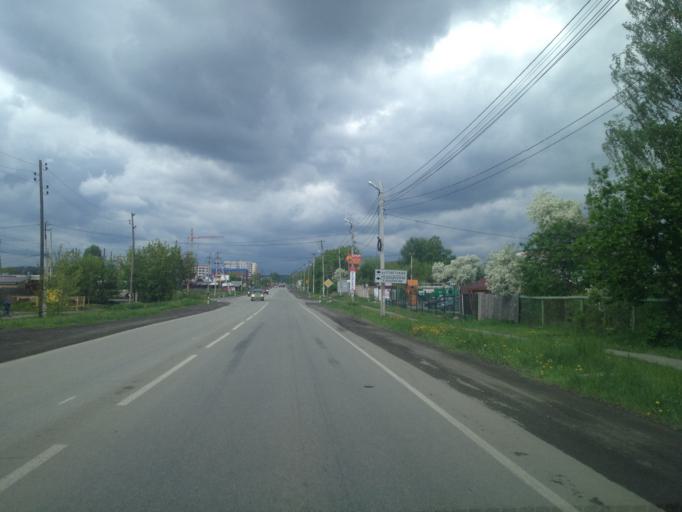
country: RU
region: Sverdlovsk
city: Aramil
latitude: 56.6973
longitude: 60.8101
